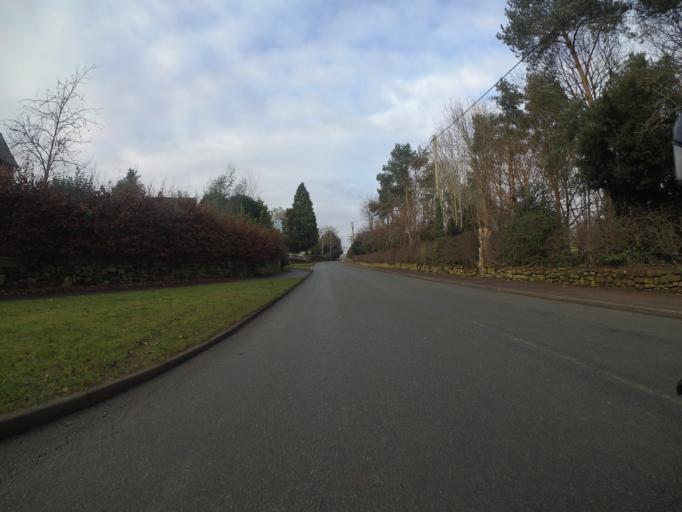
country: GB
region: England
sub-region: Cheshire West and Chester
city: Tiverton
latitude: 53.1171
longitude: -2.6542
